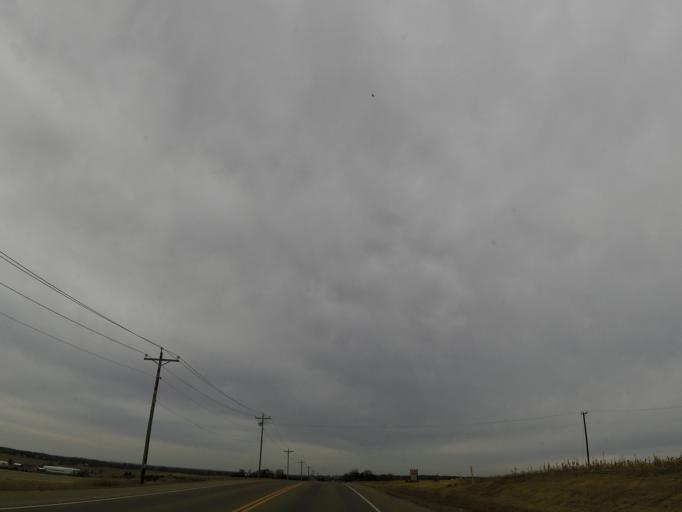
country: US
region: Minnesota
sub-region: Washington County
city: Afton
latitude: 44.8477
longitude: -92.8528
